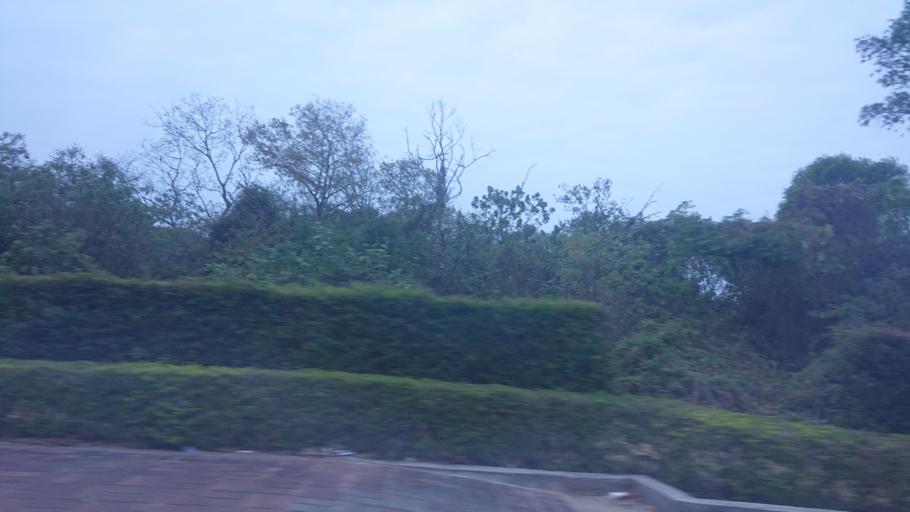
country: TW
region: Fukien
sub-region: Kinmen
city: Jincheng
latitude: 24.4439
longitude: 118.3116
